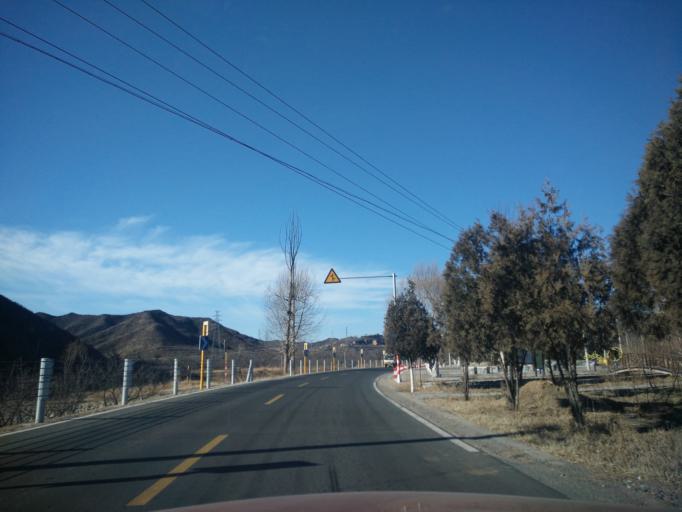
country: CN
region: Beijing
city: Zhaitang
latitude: 39.9845
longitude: 115.7466
